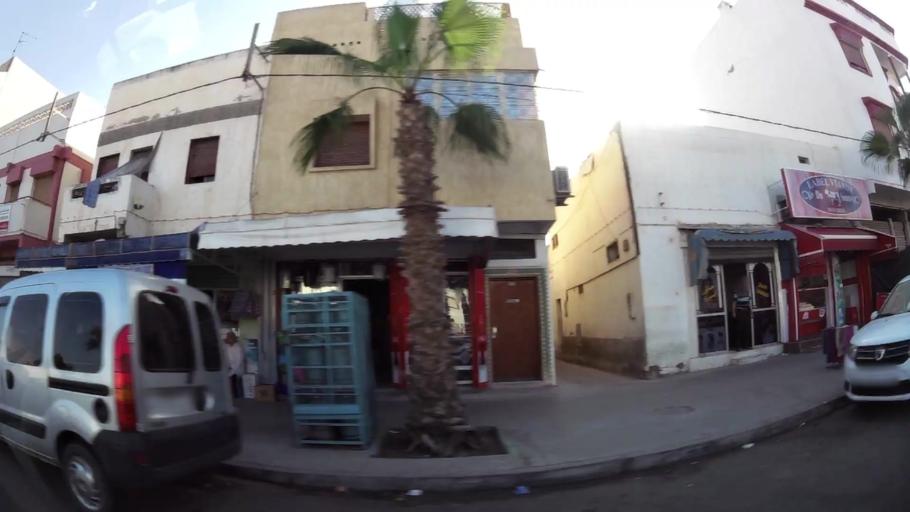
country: MA
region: Souss-Massa-Draa
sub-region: Agadir-Ida-ou-Tnan
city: Agadir
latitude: 30.4134
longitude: -9.5902
